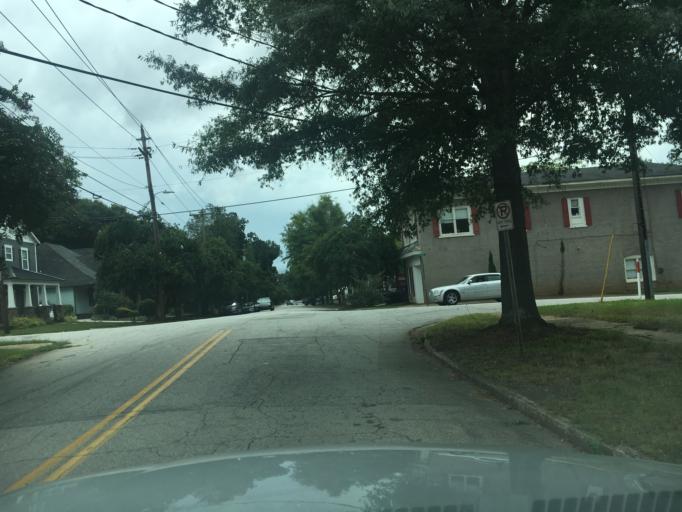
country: US
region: South Carolina
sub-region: Greenville County
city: City View
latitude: 34.8619
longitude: -82.4122
